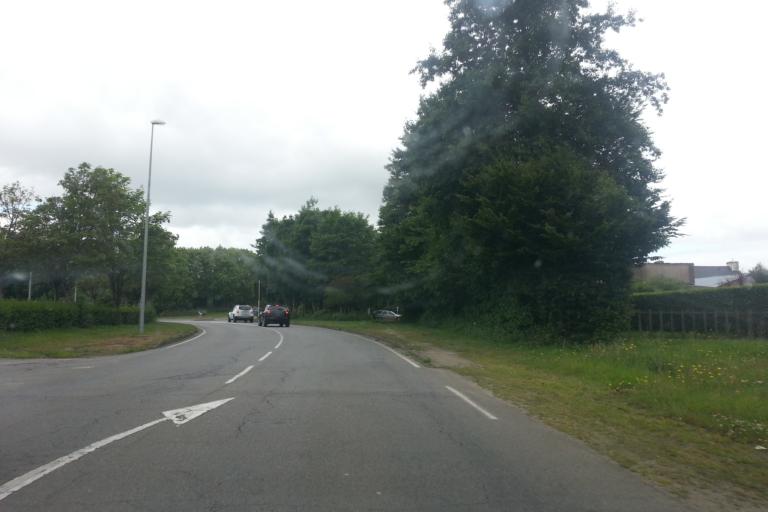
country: FR
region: Brittany
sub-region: Departement du Finistere
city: Briec
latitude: 48.0970
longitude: -4.0000
